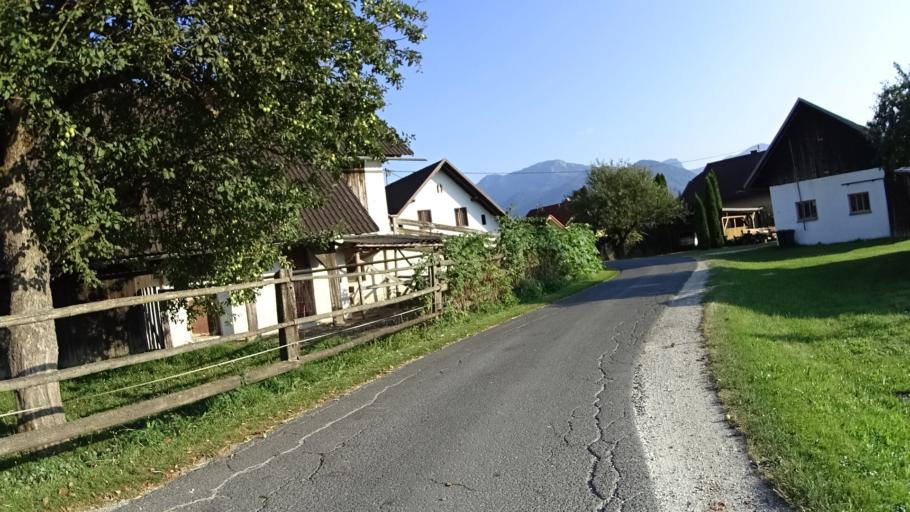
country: AT
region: Carinthia
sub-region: Politischer Bezirk Villach Land
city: Sankt Jakob
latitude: 46.5649
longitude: 14.0581
